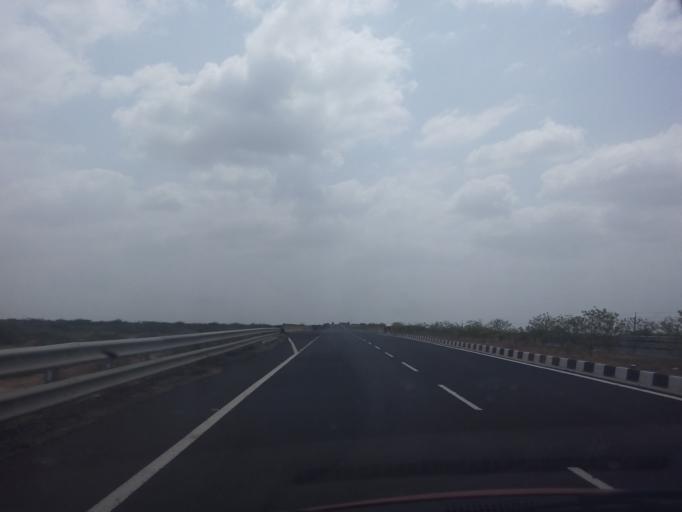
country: IN
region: Gujarat
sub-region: Surendranagar
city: Dhrangadhra
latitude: 23.0255
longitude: 71.6406
